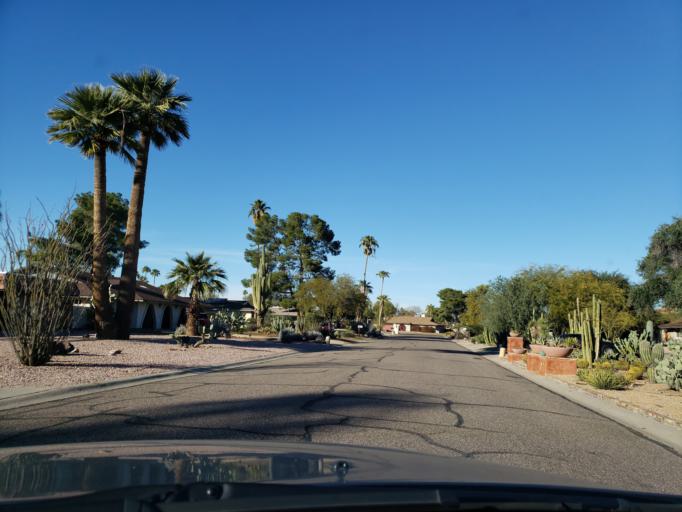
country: US
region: Arizona
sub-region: Maricopa County
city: Paradise Valley
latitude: 33.5874
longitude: -112.0059
